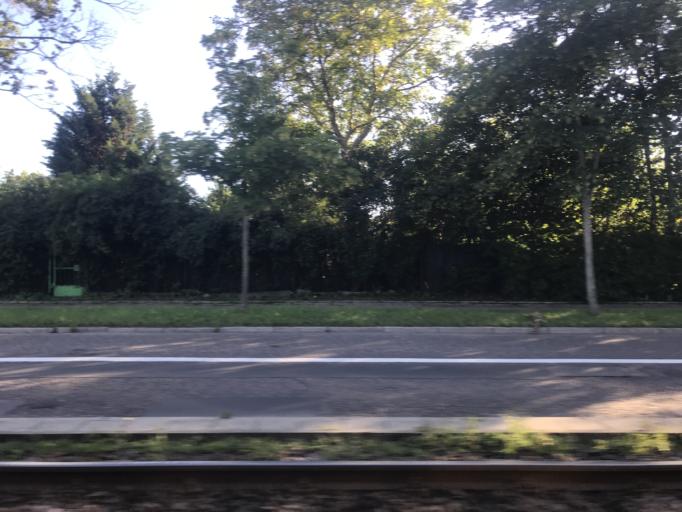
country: PL
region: Pomeranian Voivodeship
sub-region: Sopot
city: Sopot
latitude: 54.3935
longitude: 18.5745
